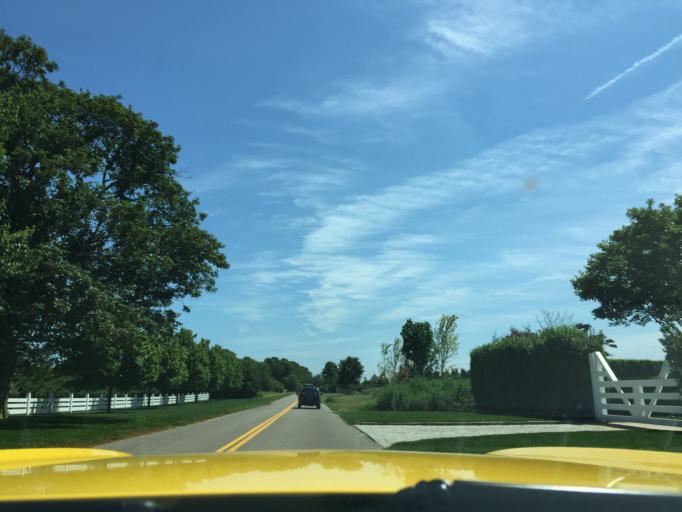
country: US
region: New York
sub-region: Suffolk County
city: Bridgehampton
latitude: 40.9361
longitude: -72.2617
